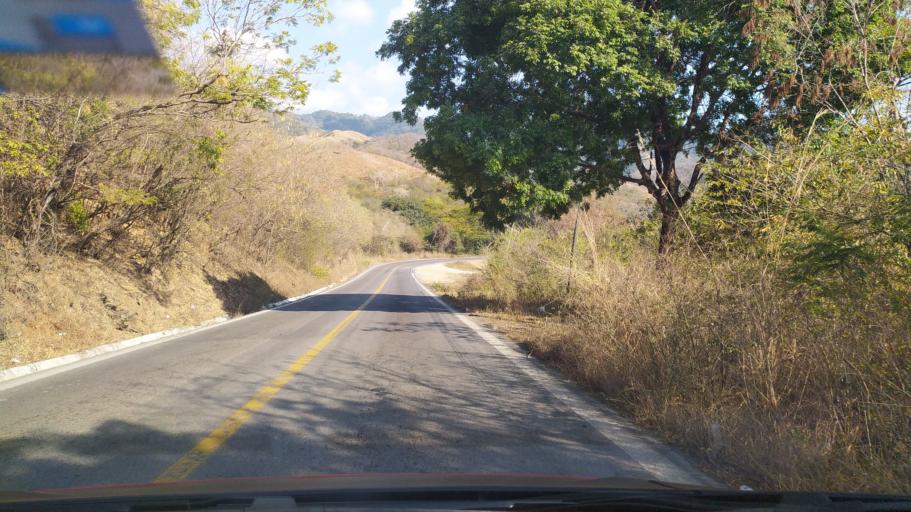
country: MX
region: Michoacan
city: Coahuayana Viejo
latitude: 18.5941
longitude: -103.6741
